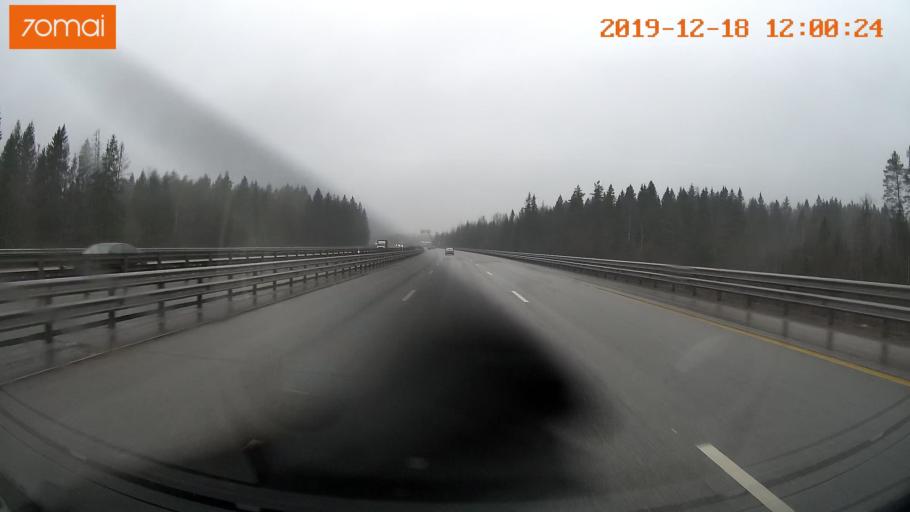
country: RU
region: Moskovskaya
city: Yershovo
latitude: 55.8450
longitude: 36.8218
